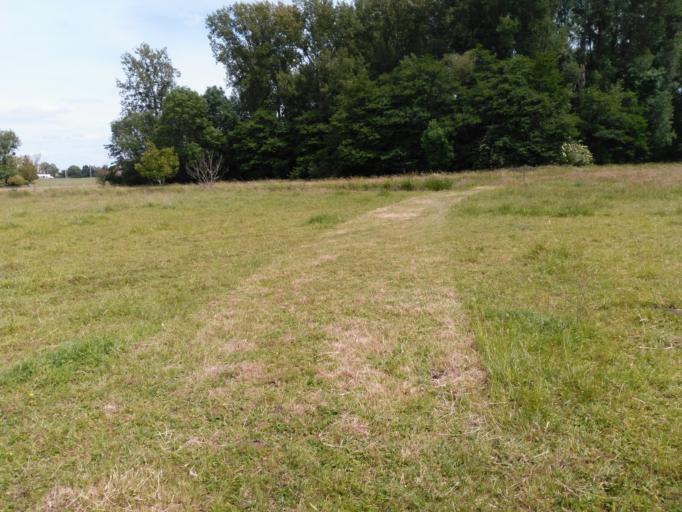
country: BE
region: Flanders
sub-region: Provincie Vlaams-Brabant
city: Bierbeek
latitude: 50.8591
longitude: 4.7658
